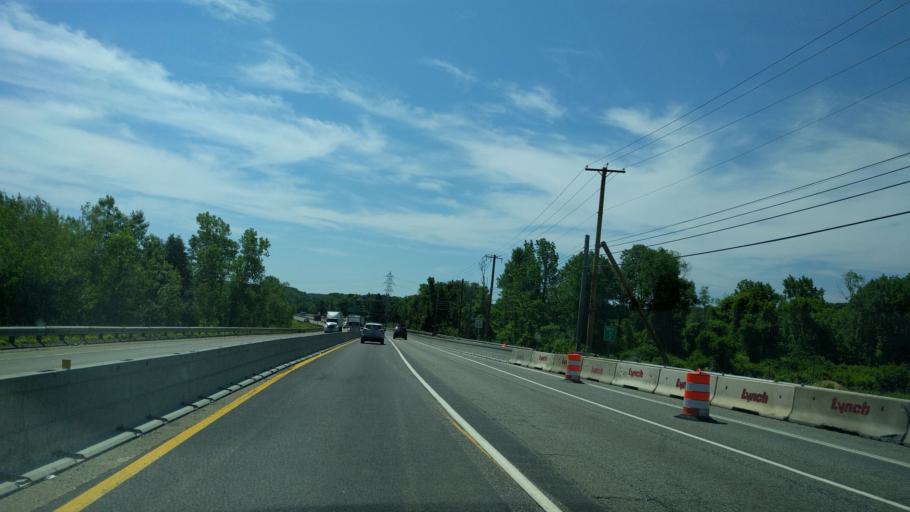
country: US
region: Massachusetts
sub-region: Worcester County
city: Millbury
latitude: 42.1909
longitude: -71.7695
